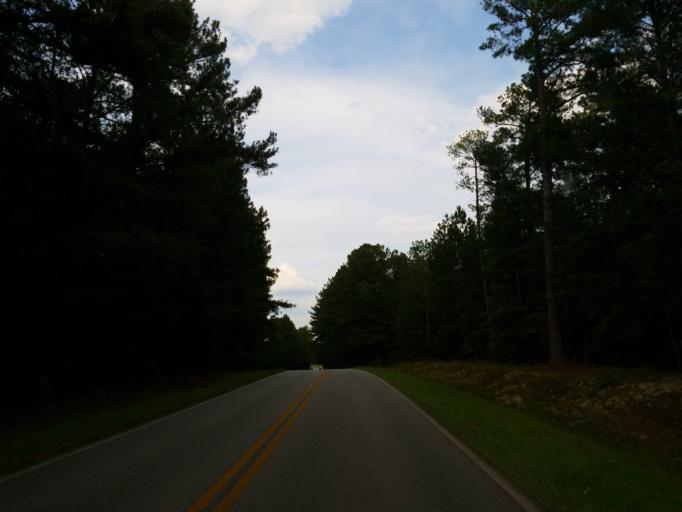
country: US
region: Georgia
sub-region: Butts County
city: Indian Springs
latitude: 33.1637
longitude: -84.0438
